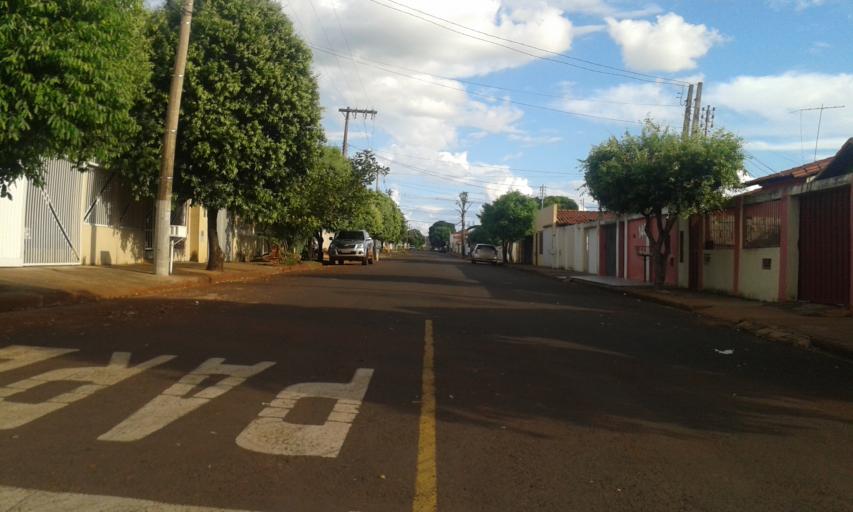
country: BR
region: Minas Gerais
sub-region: Ituiutaba
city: Ituiutaba
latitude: -18.9640
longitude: -49.4585
